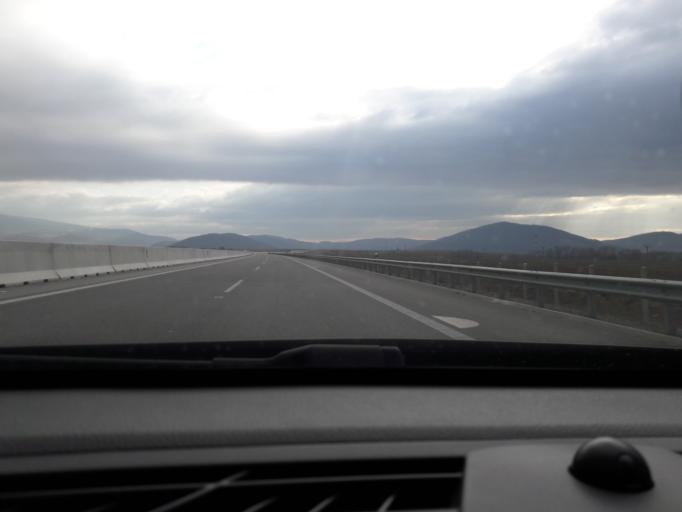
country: SK
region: Banskobystricky
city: Hrochot,Slovakia
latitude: 48.5701
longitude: 19.2846
